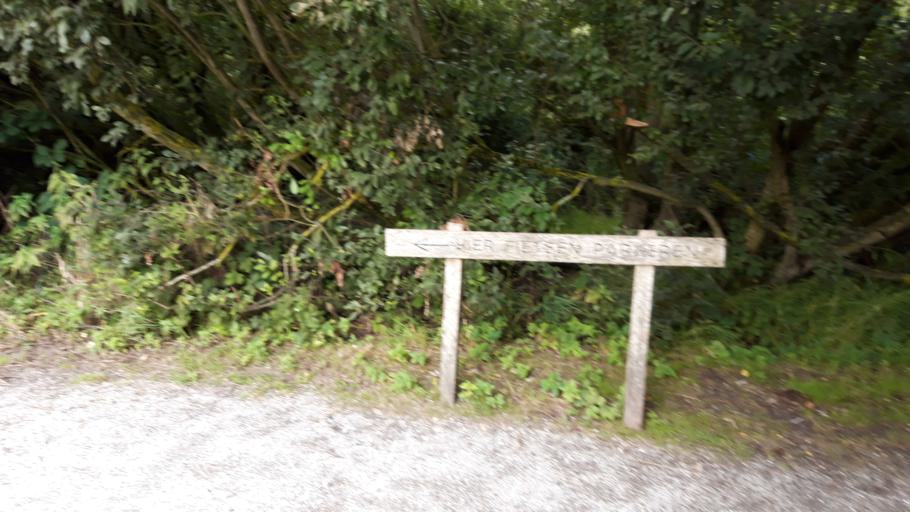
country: NL
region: Friesland
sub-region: Gemeente Schiermonnikoog
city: Schiermonnikoog
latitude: 53.4713
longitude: 6.1509
